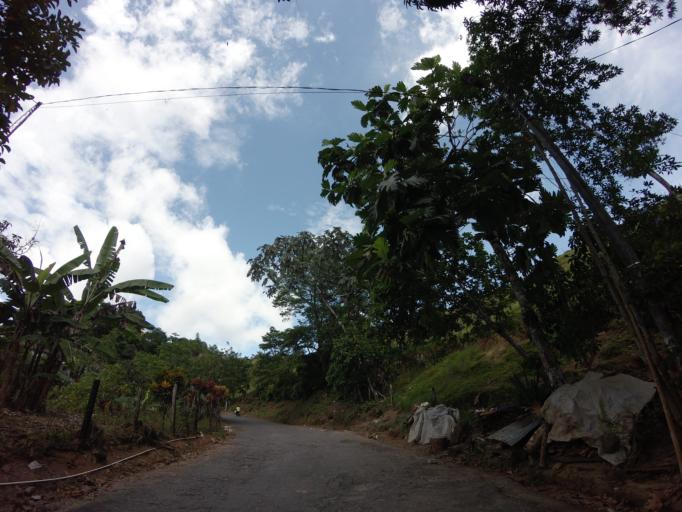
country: CO
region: Caldas
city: Norcasia
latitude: 5.5789
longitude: -74.8848
